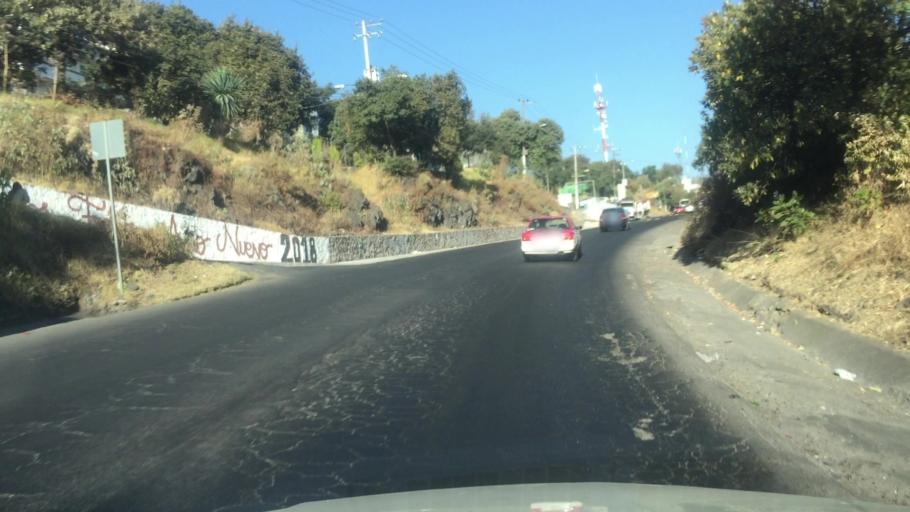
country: MX
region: Mexico City
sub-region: Tlalpan
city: Lomas de Tepemecatl
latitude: 19.2655
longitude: -99.2063
